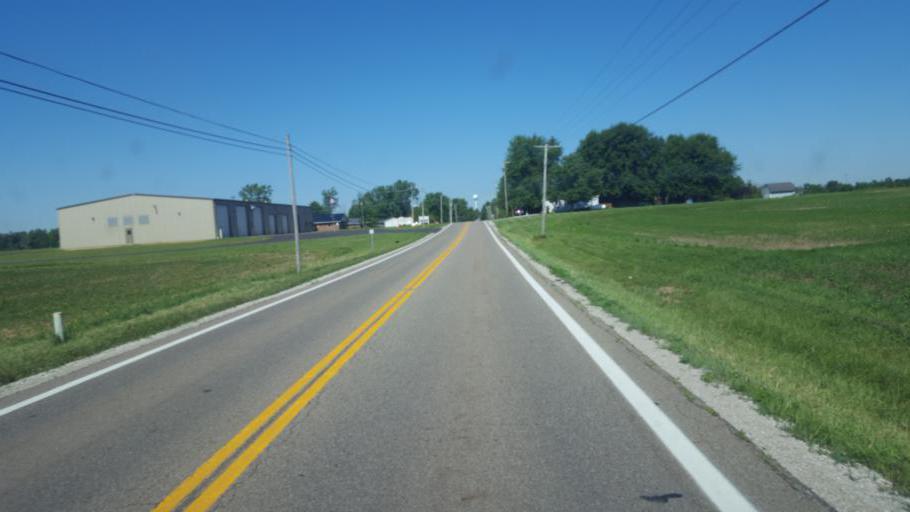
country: US
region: Ohio
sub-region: Morrow County
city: Cardington
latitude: 40.4017
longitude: -82.7975
